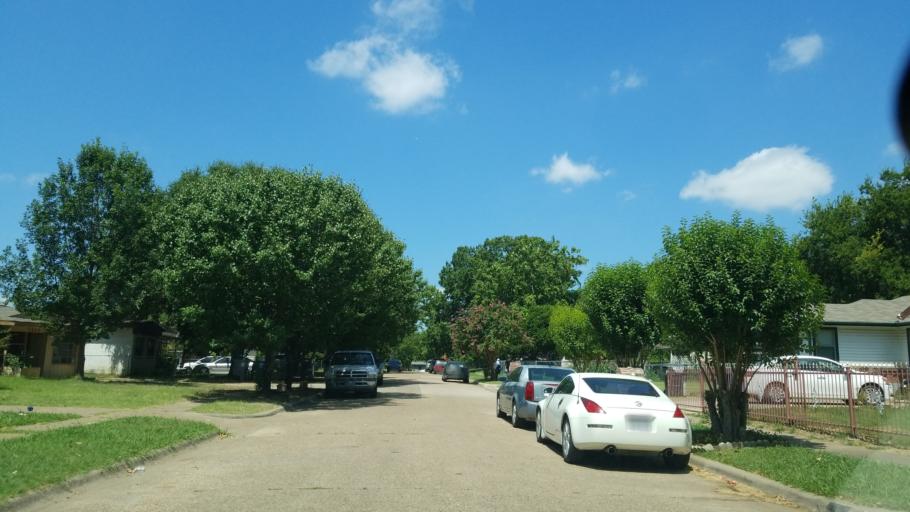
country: US
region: Texas
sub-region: Dallas County
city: Balch Springs
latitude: 32.7373
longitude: -96.6969
